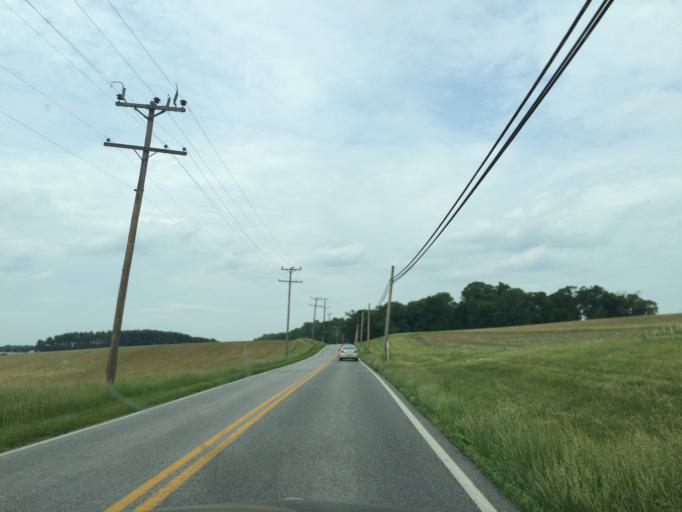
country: US
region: Maryland
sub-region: Howard County
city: Highland
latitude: 39.2587
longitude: -76.9260
